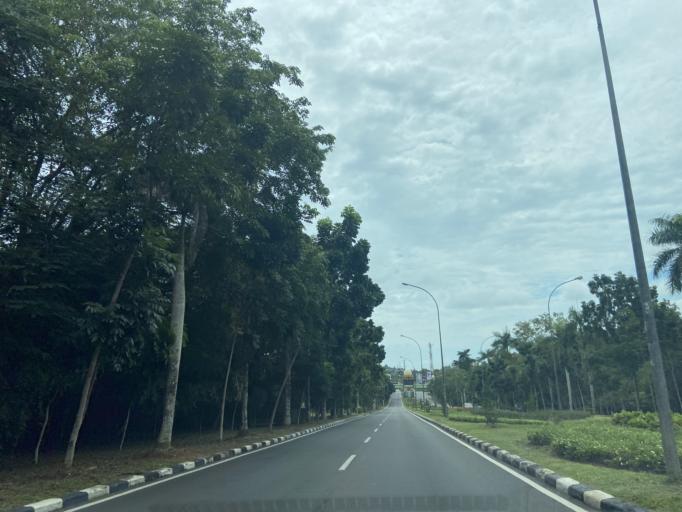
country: SG
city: Singapore
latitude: 1.1249
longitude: 104.1104
